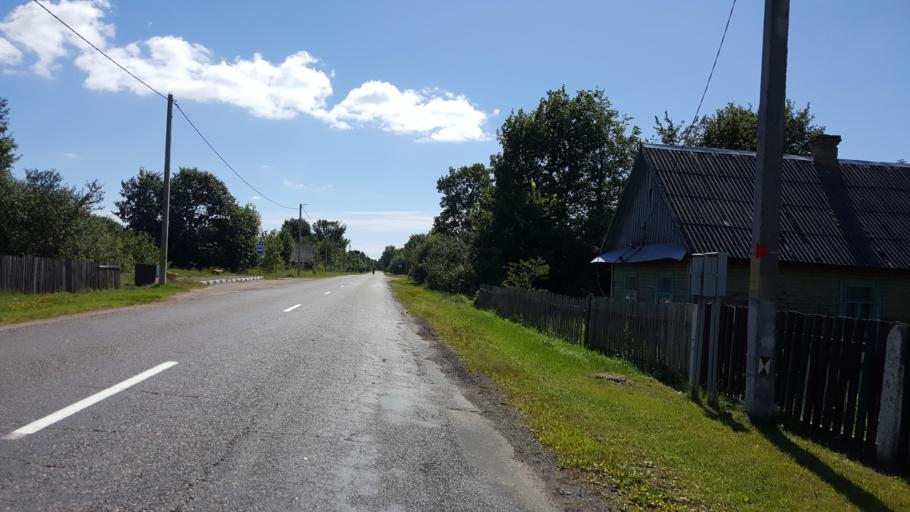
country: BY
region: Brest
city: Zhabinka
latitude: 52.3664
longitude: 24.1445
